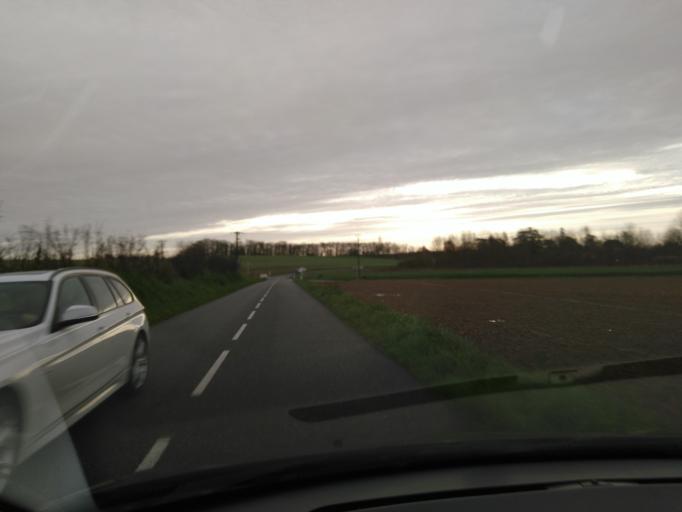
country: FR
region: Midi-Pyrenees
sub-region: Departement de la Haute-Garonne
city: Labastide-Saint-Sernin
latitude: 43.7489
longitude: 1.4739
